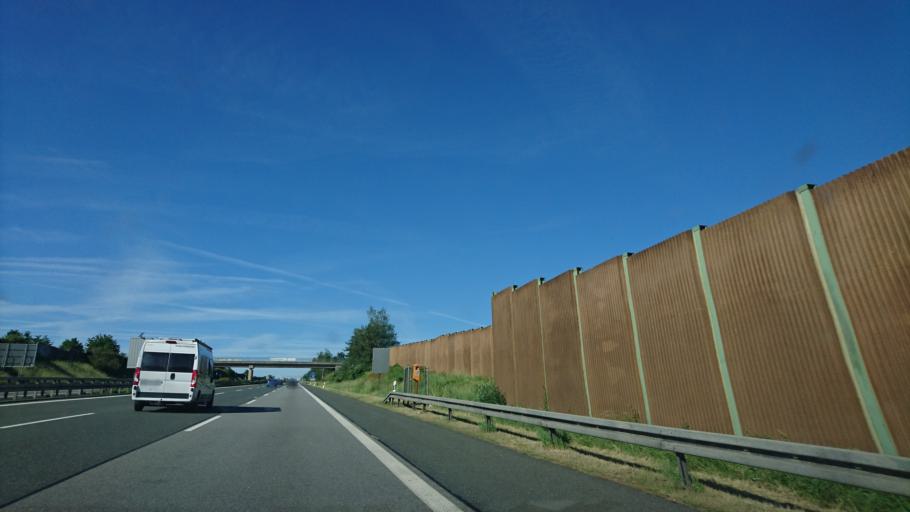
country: DE
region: Saxony
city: Wilkau-Hasslau
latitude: 50.6600
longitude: 12.5079
